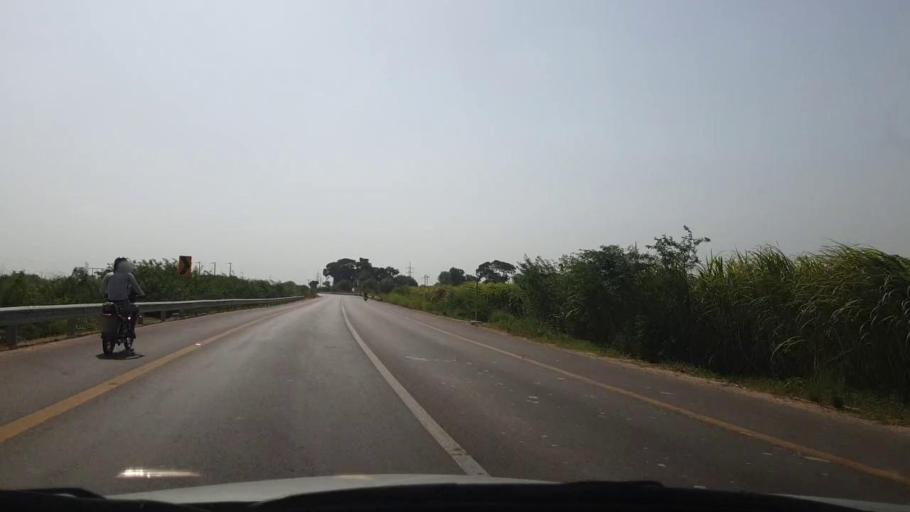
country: PK
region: Sindh
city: Matli
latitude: 25.0827
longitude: 68.6077
